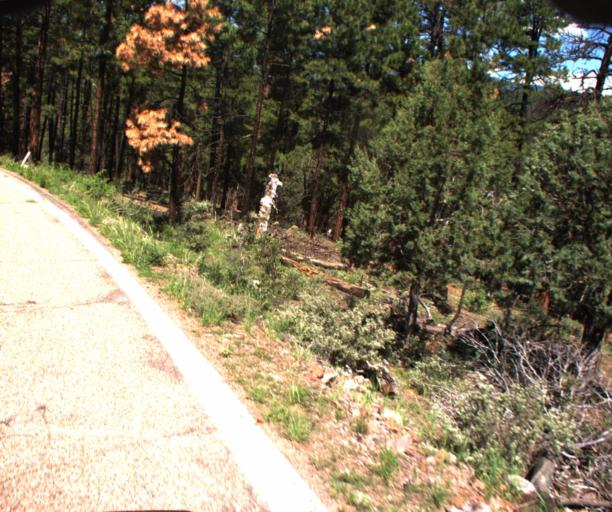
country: US
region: Arizona
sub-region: Greenlee County
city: Morenci
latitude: 33.5264
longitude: -109.3079
